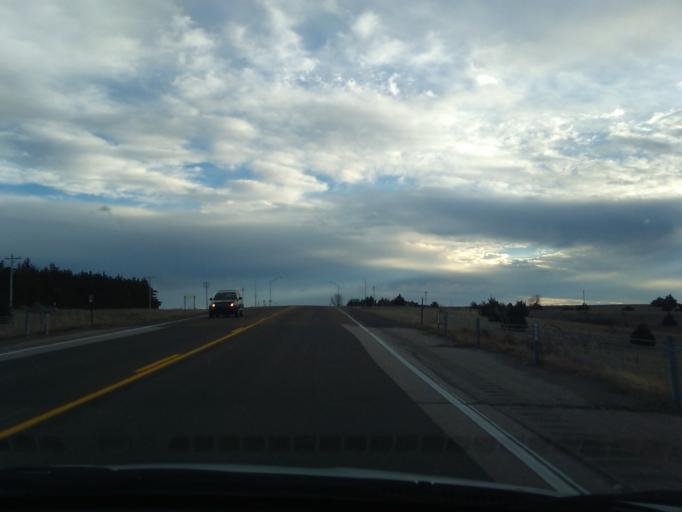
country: US
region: Nebraska
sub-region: Phelps County
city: Holdrege
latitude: 40.3097
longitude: -99.3684
